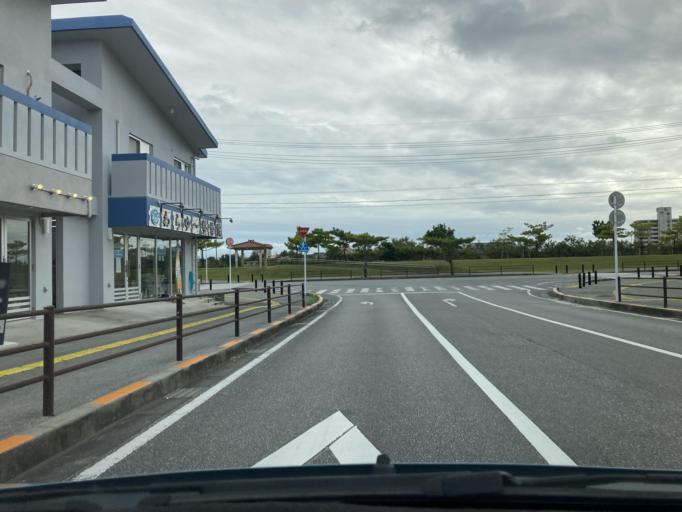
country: JP
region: Okinawa
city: Itoman
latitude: 26.1532
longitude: 127.6629
